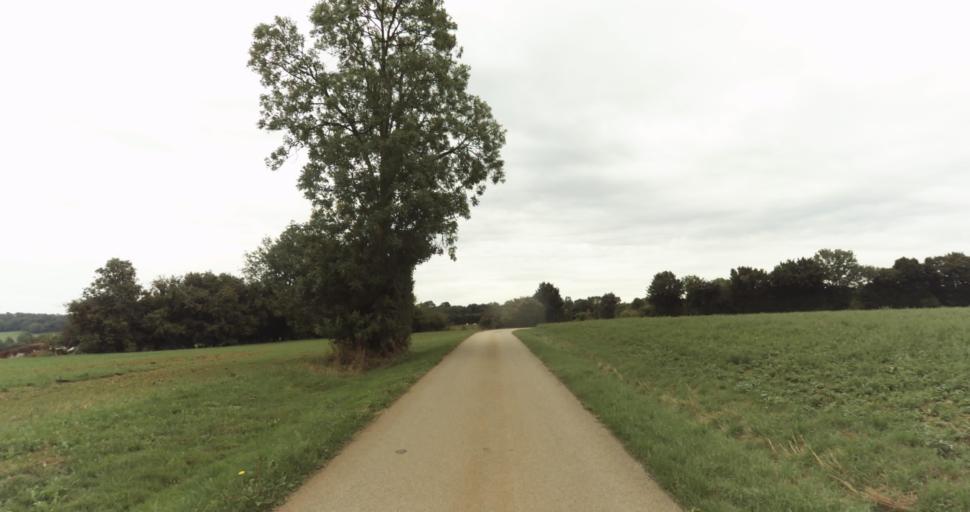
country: FR
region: Lower Normandy
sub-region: Departement de l'Orne
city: Gace
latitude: 48.7386
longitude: 0.3351
